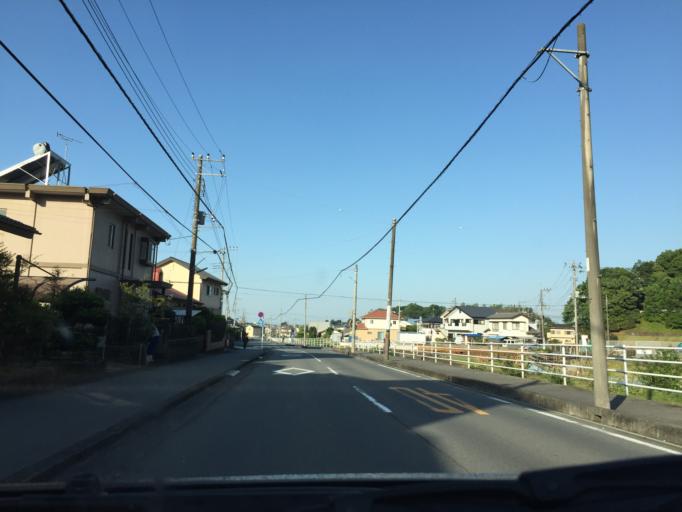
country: JP
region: Shizuoka
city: Mishima
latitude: 35.1753
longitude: 138.9255
